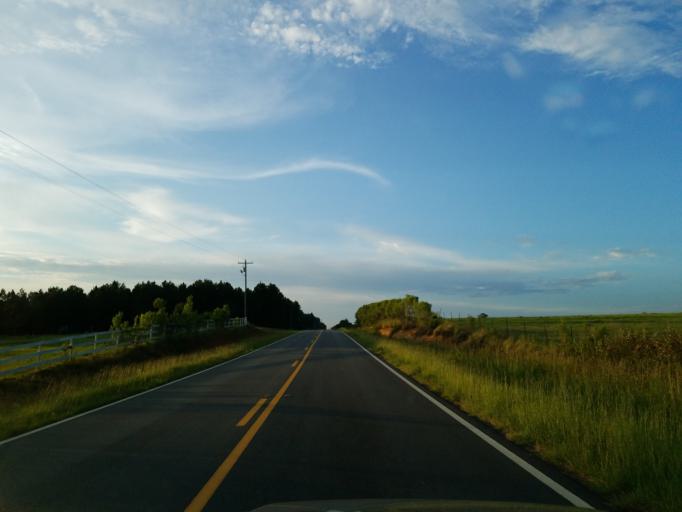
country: US
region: Georgia
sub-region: Turner County
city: Ashburn
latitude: 31.6481
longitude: -83.5663
